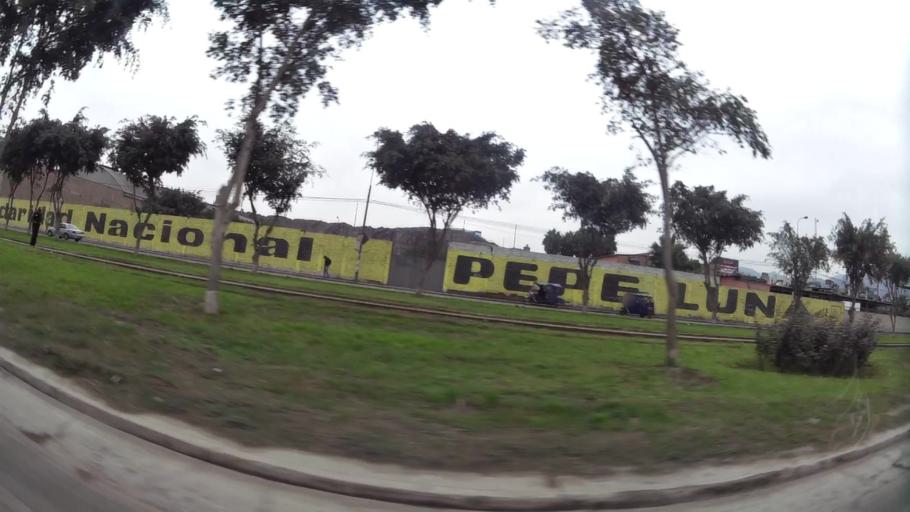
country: PE
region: Lima
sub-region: Lima
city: Vitarte
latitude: -12.0472
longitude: -76.9502
